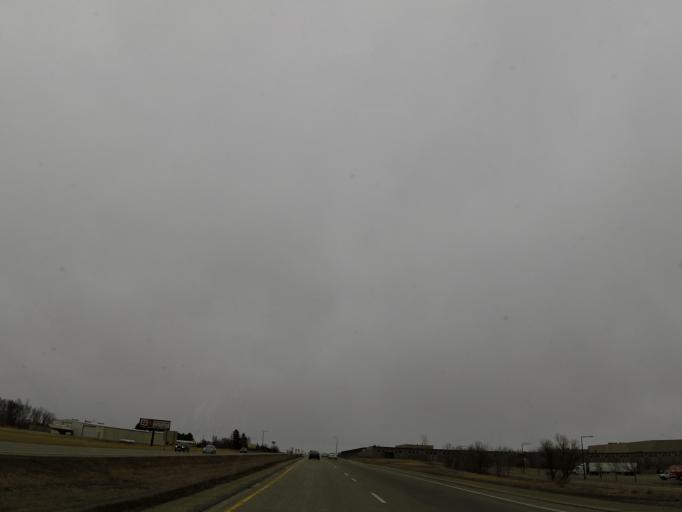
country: US
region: Minnesota
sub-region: Le Sueur County
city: Le Sueur
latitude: 44.4887
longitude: -93.8776
